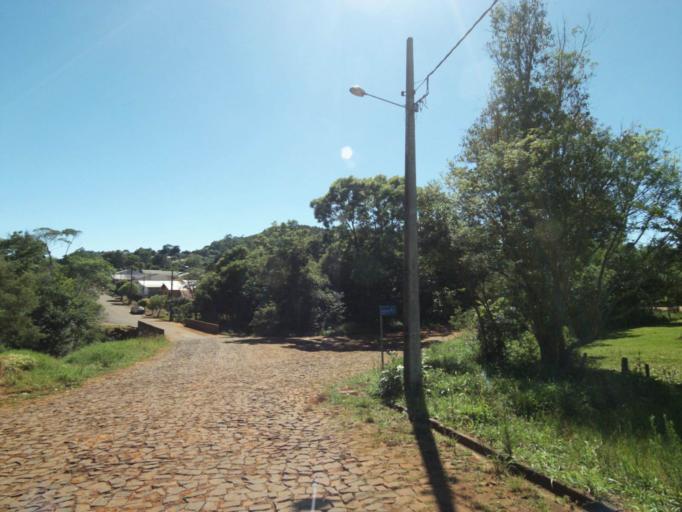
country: BR
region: Santa Catarina
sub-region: Sao Lourenco Do Oeste
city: Sao Lourenco dOeste
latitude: -26.2701
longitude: -52.7792
